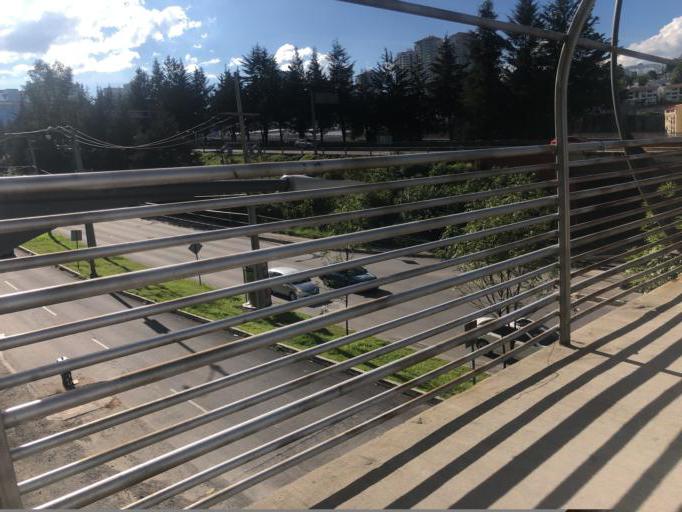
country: MX
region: Mexico City
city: Col. Bosques de las Lomas
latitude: 19.3617
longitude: -99.2687
